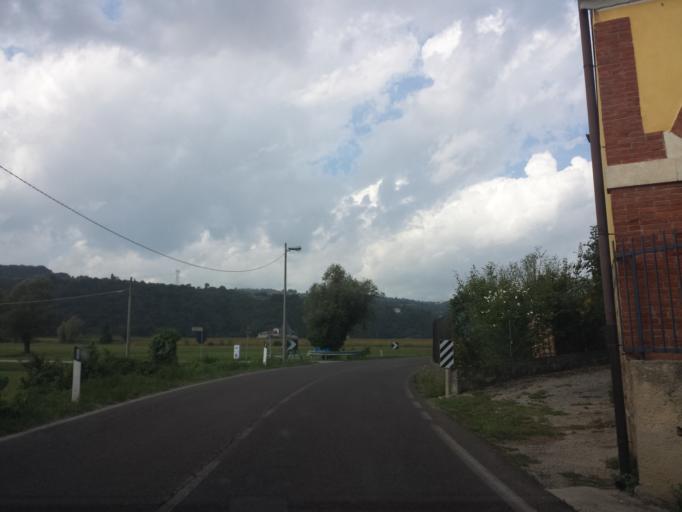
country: IT
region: Veneto
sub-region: Provincia di Vicenza
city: Sovizzo
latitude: 45.5460
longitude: 11.4311
